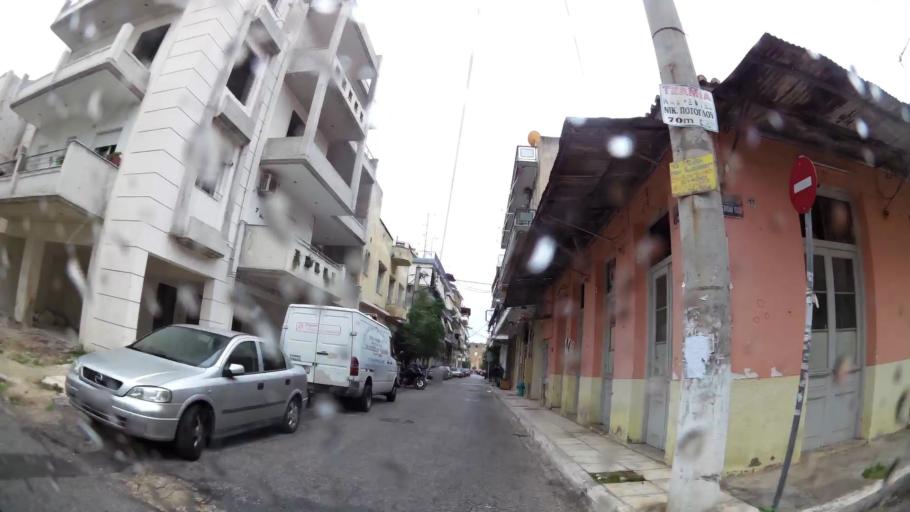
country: GR
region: Attica
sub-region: Nomos Piraios
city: Nikaia
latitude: 37.9625
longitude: 23.6523
